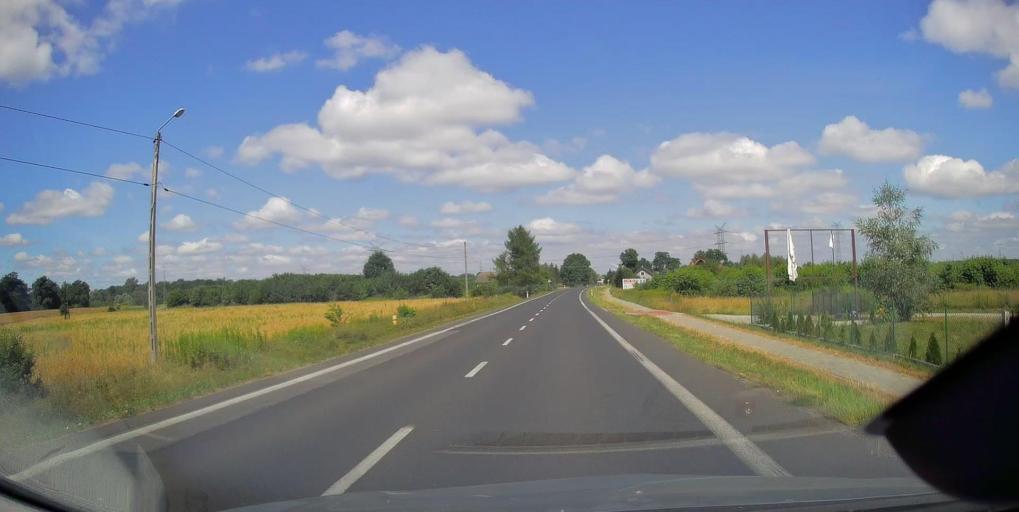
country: PL
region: Subcarpathian Voivodeship
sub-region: Powiat debicki
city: Brzeznica
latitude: 50.1229
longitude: 21.4876
